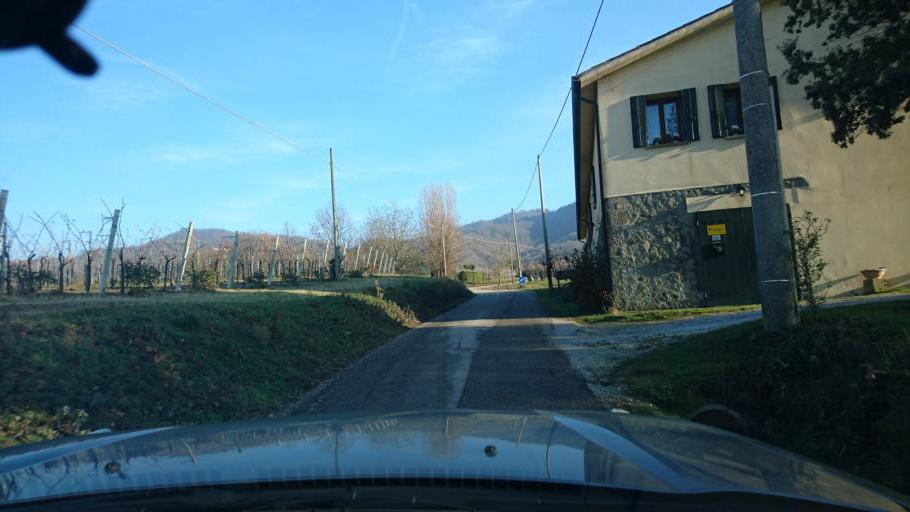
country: IT
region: Veneto
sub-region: Provincia di Padova
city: Vo
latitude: 45.3227
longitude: 11.6706
